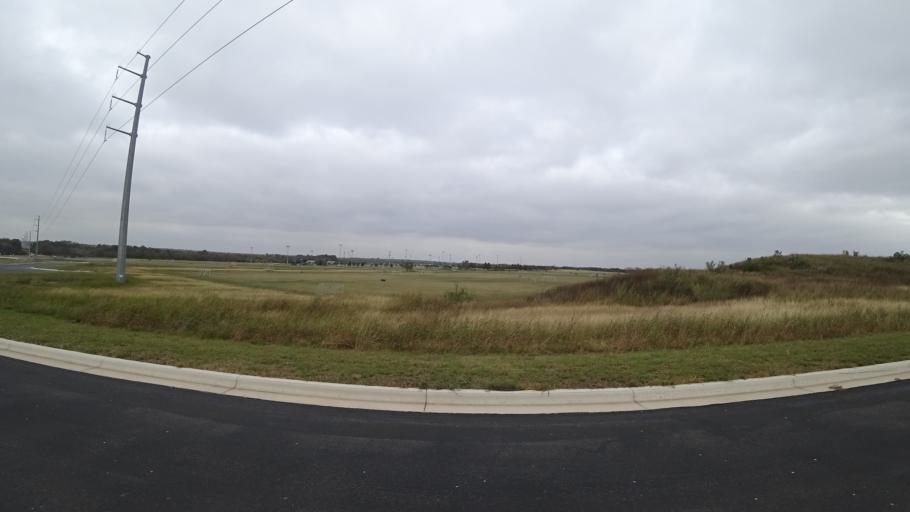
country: US
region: Texas
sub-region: Travis County
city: Pflugerville
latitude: 30.4091
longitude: -97.5930
